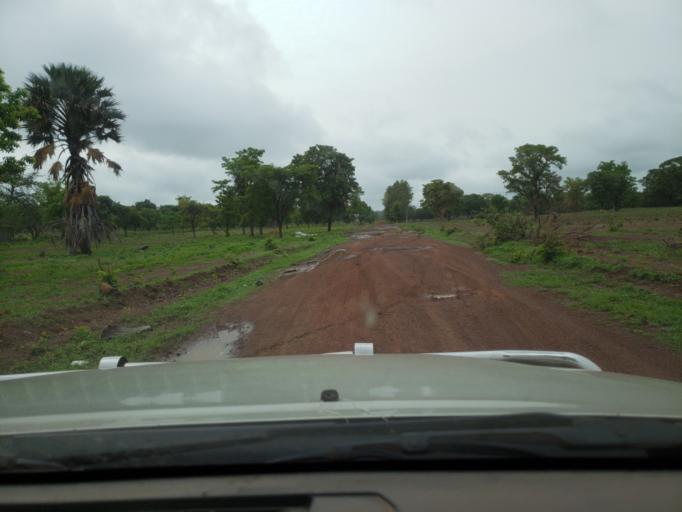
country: ML
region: Koulikoro
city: Kangaba
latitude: 12.0240
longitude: -8.7306
